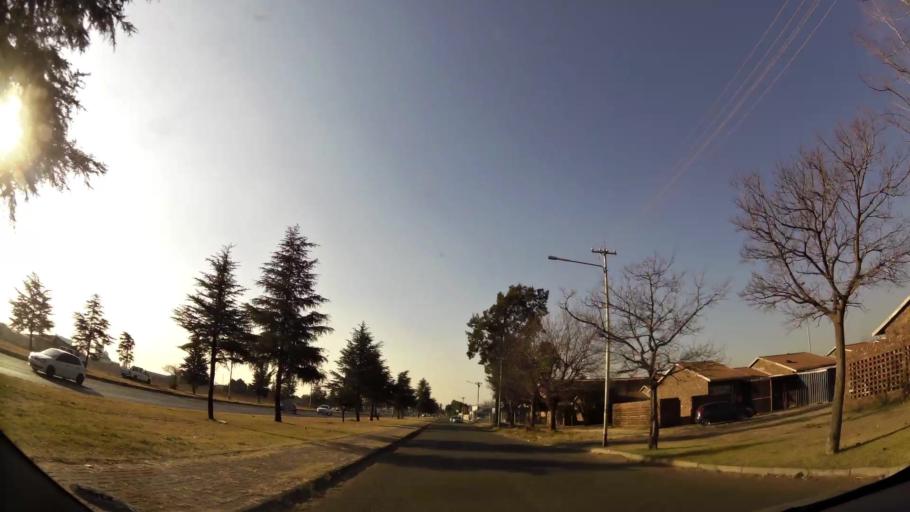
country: ZA
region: Gauteng
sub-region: West Rand District Municipality
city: Randfontein
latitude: -26.1971
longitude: 27.6996
